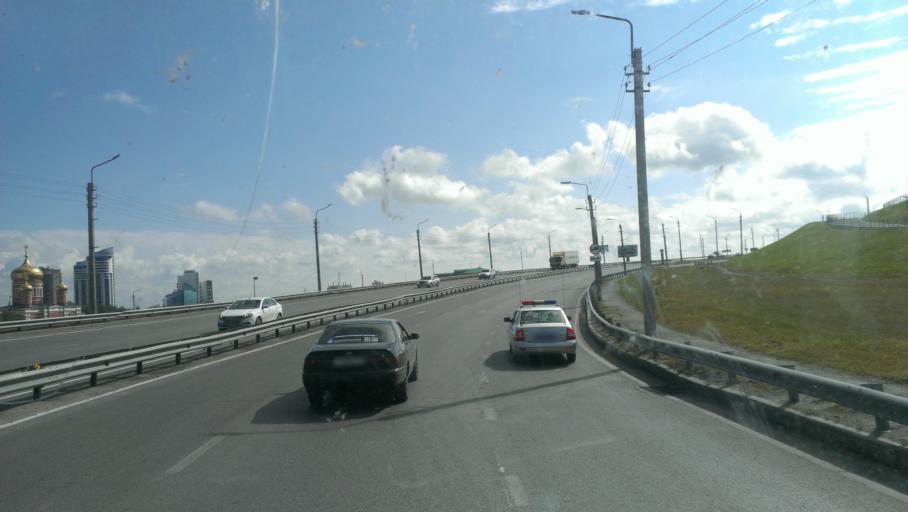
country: RU
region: Altai Krai
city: Zaton
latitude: 53.3260
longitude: 83.7939
